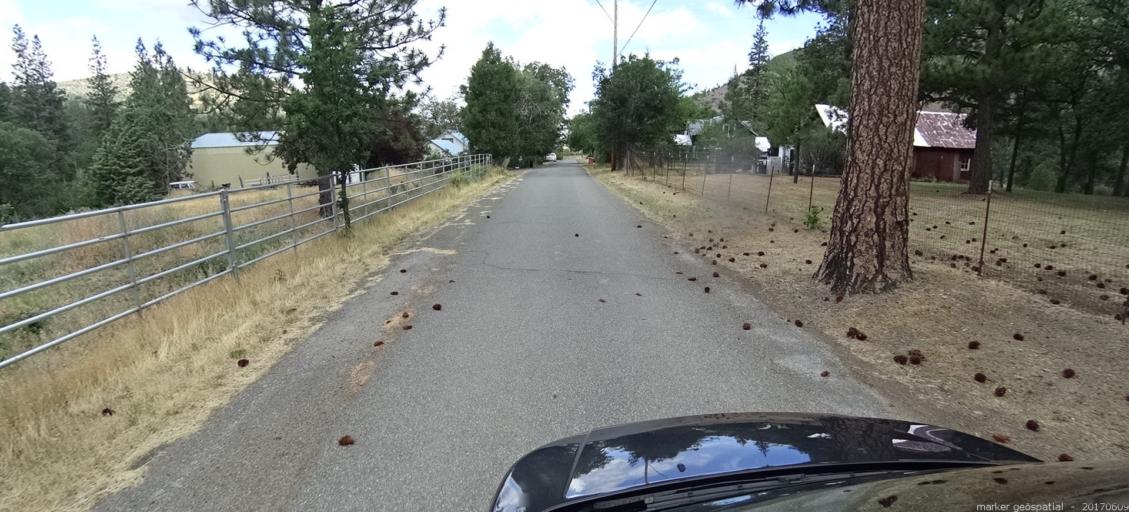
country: US
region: California
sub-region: Siskiyou County
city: Weed
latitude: 41.3056
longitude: -122.7988
